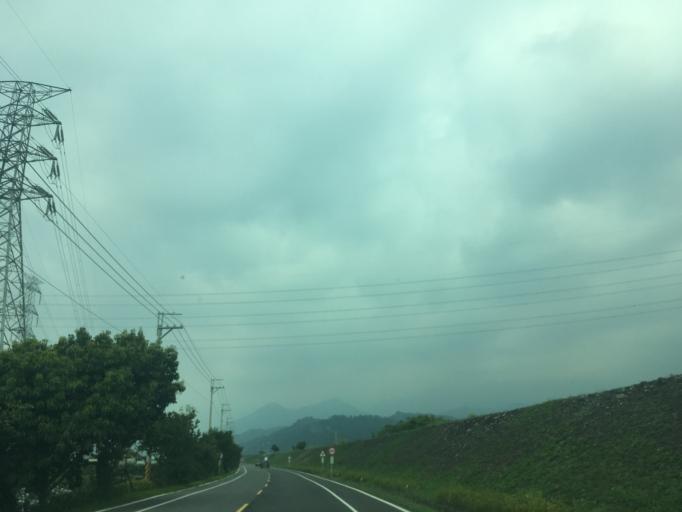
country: TW
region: Taiwan
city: Fengyuan
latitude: 24.2893
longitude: 120.8500
